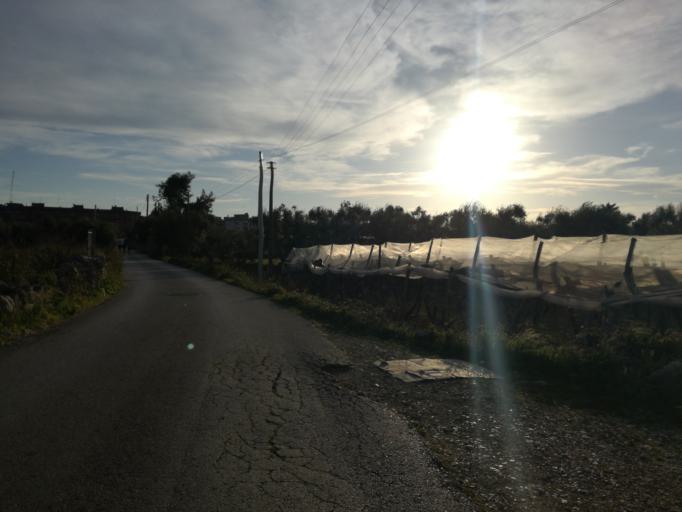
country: IT
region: Apulia
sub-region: Provincia di Bari
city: Valenzano
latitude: 41.0497
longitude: 16.8911
